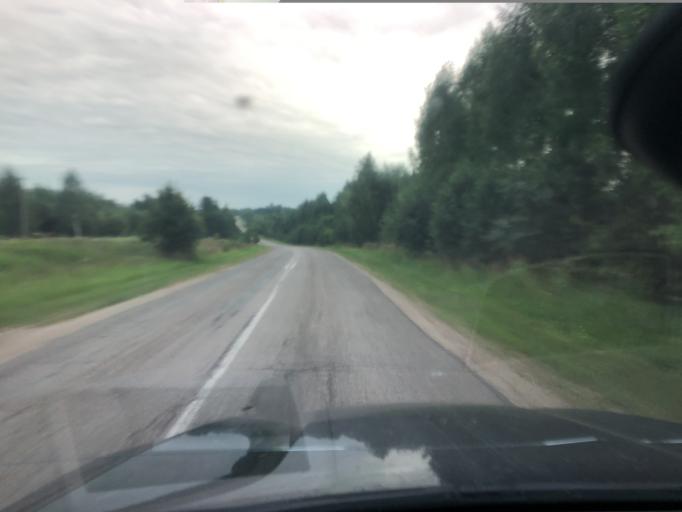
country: RU
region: Jaroslavl
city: Petrovsk
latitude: 56.9963
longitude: 39.1035
